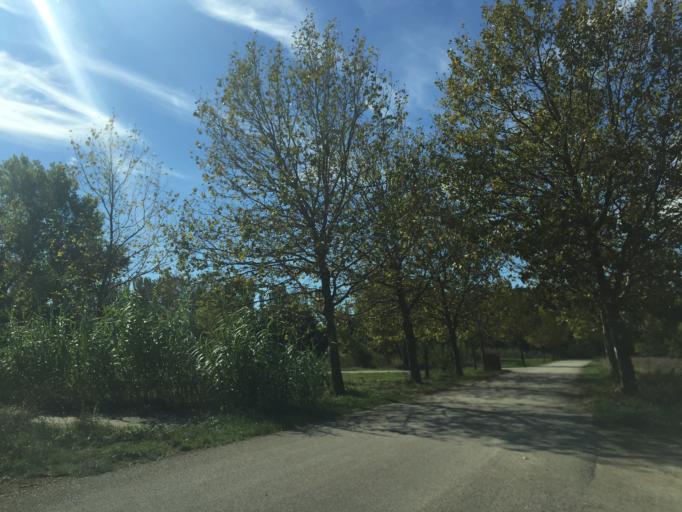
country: FR
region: Provence-Alpes-Cote d'Azur
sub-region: Departement du Vaucluse
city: Piolenc
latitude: 44.1586
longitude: 4.7286
